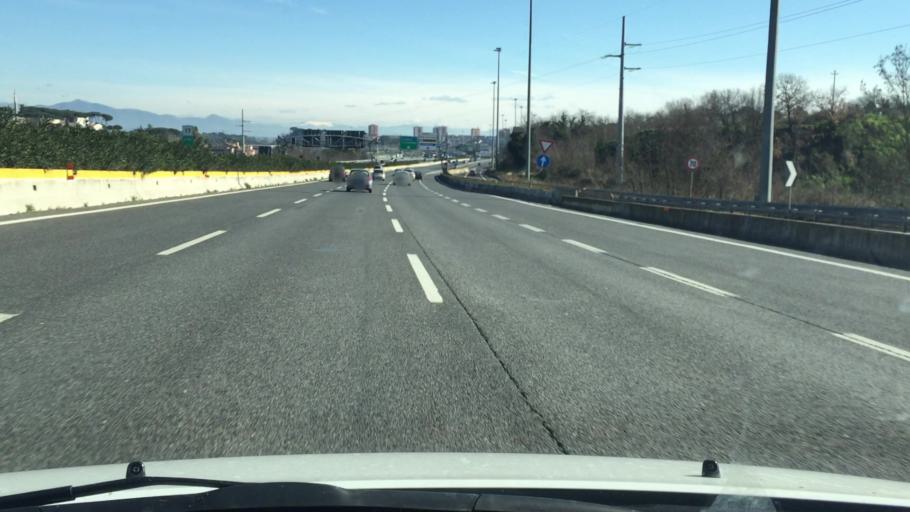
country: IT
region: Latium
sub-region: Citta metropolitana di Roma Capitale
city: Monte Caminetto
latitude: 41.9864
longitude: 12.4798
